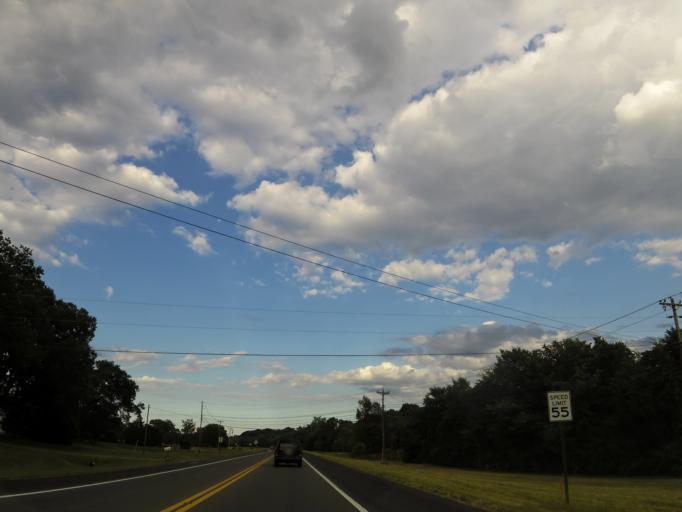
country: US
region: Tennessee
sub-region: Maury County
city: Columbia
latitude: 35.6362
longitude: -86.9902
